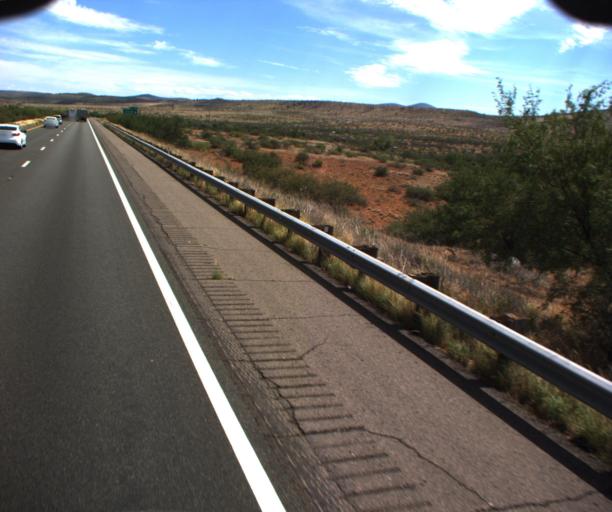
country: US
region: Arizona
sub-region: Yavapai County
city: Cordes Lakes
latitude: 34.3981
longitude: -112.0776
